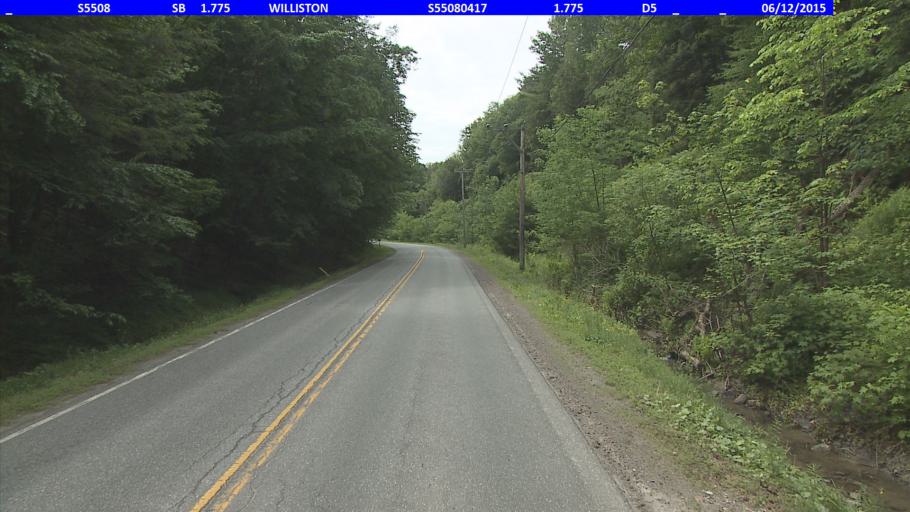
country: US
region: Vermont
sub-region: Chittenden County
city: Williston
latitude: 44.4599
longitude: -73.0565
